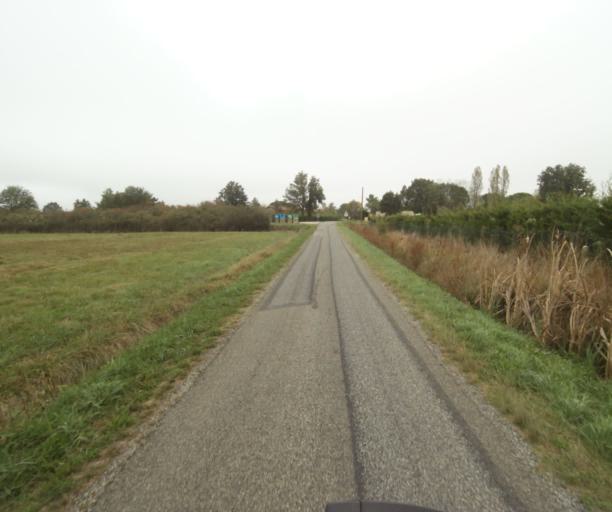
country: FR
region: Midi-Pyrenees
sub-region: Departement du Tarn-et-Garonne
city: Orgueil
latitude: 43.9044
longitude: 1.4003
